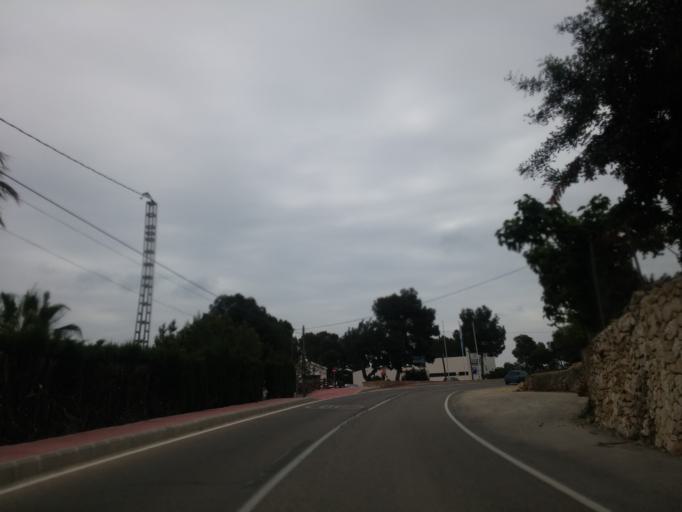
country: ES
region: Valencia
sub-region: Provincia de Alicante
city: Calp
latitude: 38.6638
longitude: 0.0869
